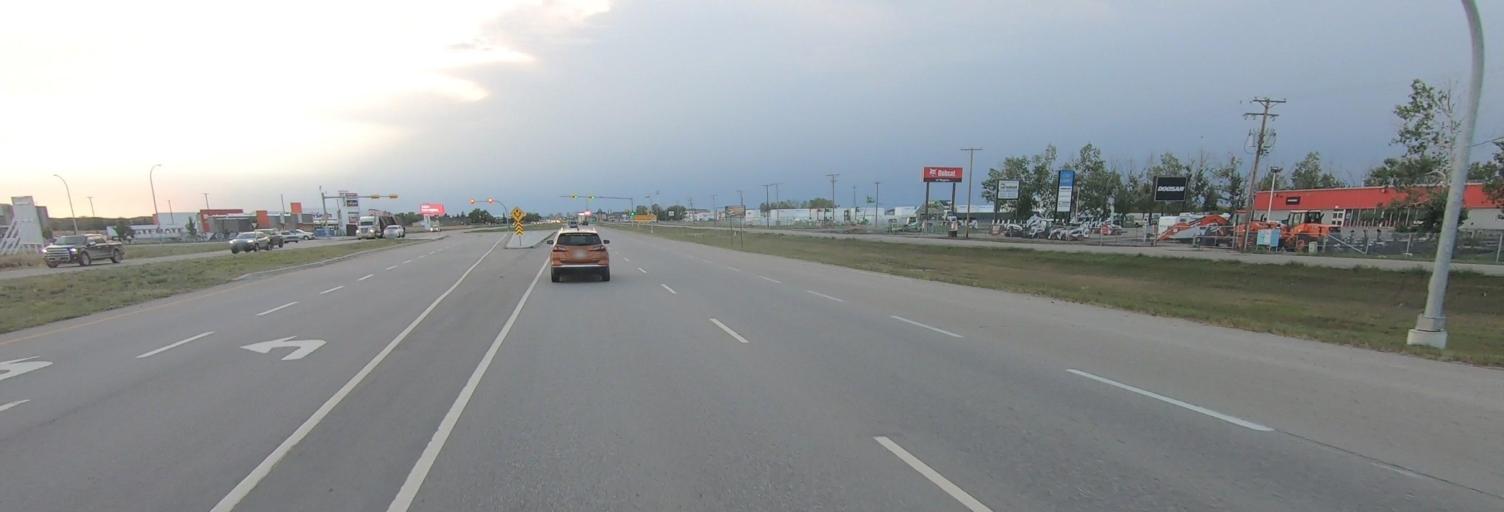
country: CA
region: Saskatchewan
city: Pilot Butte
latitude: 50.4478
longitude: -104.5096
